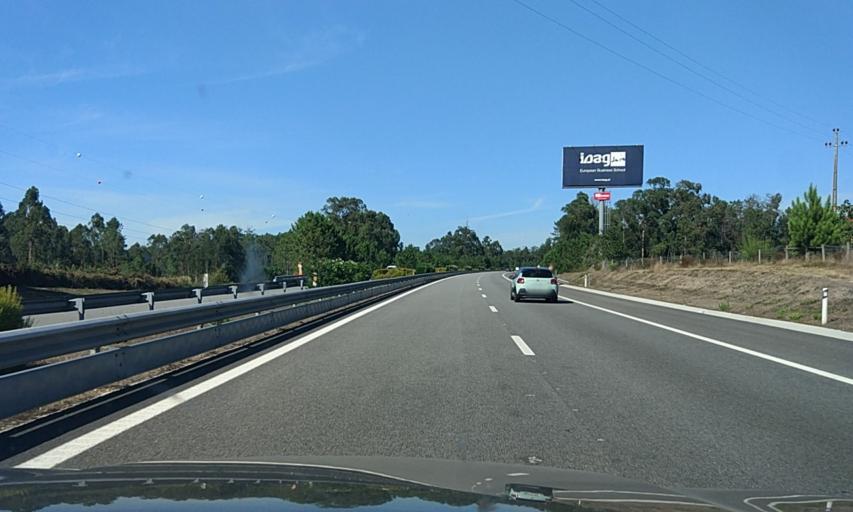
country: PT
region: Leiria
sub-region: Pombal
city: Pombal
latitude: 39.8766
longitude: -8.6991
